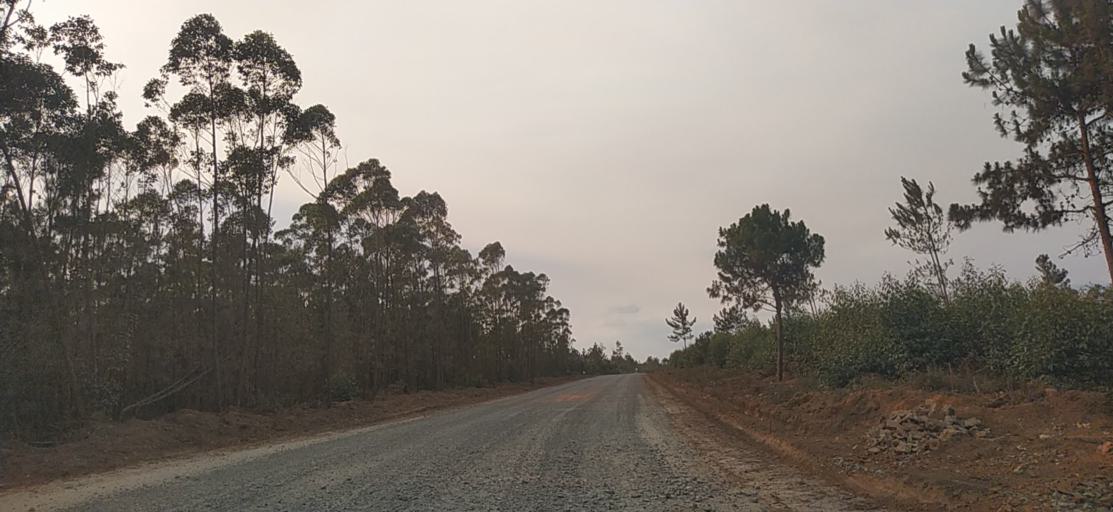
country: MG
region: Alaotra Mangoro
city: Moramanga
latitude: -18.5597
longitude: 48.2596
